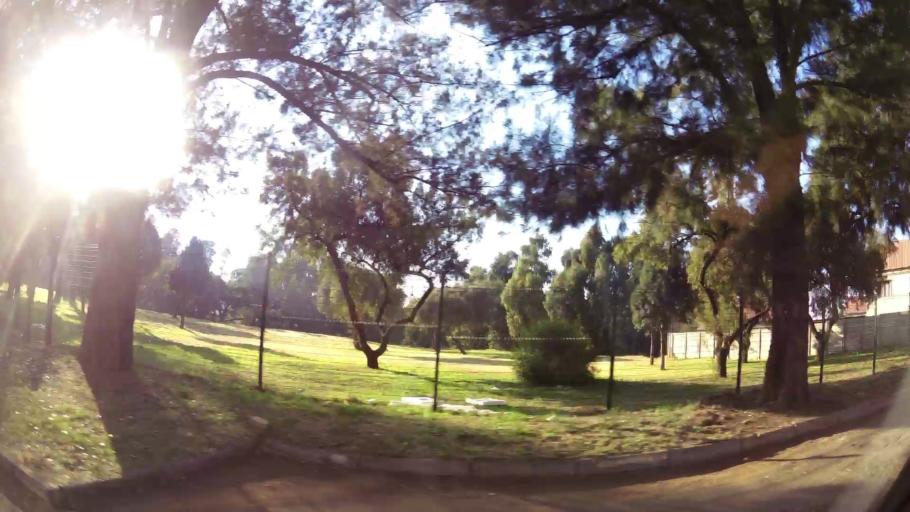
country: ZA
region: Gauteng
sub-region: Ekurhuleni Metropolitan Municipality
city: Germiston
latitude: -26.2025
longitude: 28.1323
